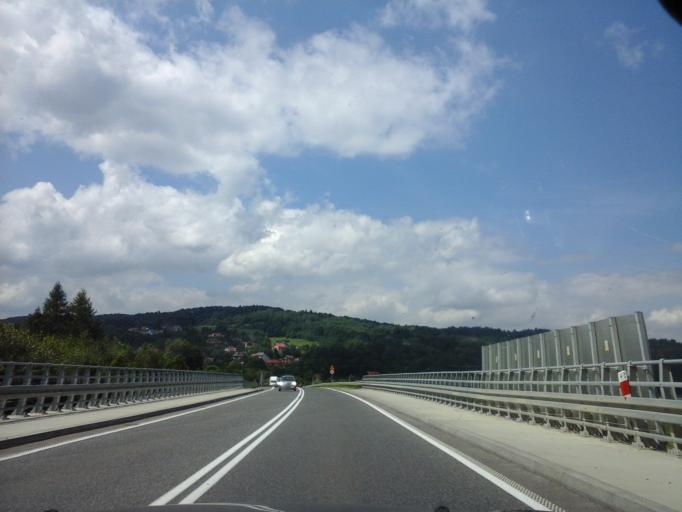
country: PL
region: Lesser Poland Voivodeship
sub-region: Powiat suski
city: Zembrzyce
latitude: 49.7808
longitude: 19.5860
